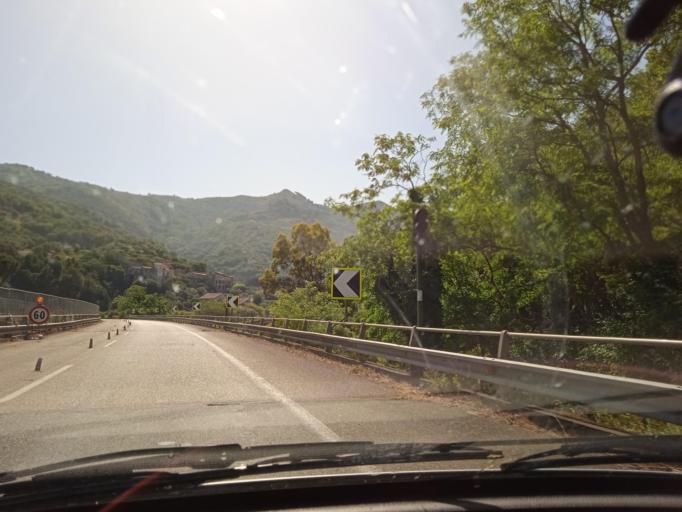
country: IT
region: Sicily
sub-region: Messina
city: Piraino
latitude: 38.1401
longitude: 14.8696
